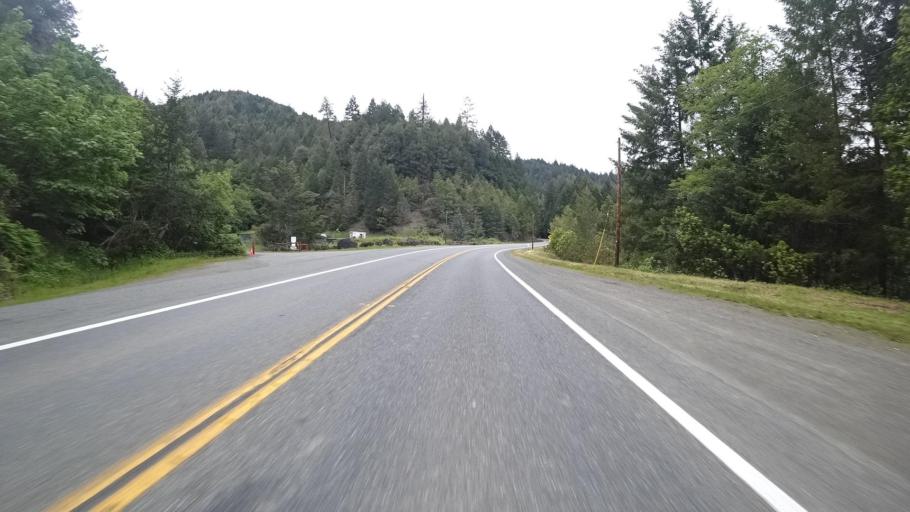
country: US
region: California
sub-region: Humboldt County
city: Willow Creek
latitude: 40.9995
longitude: -123.6457
